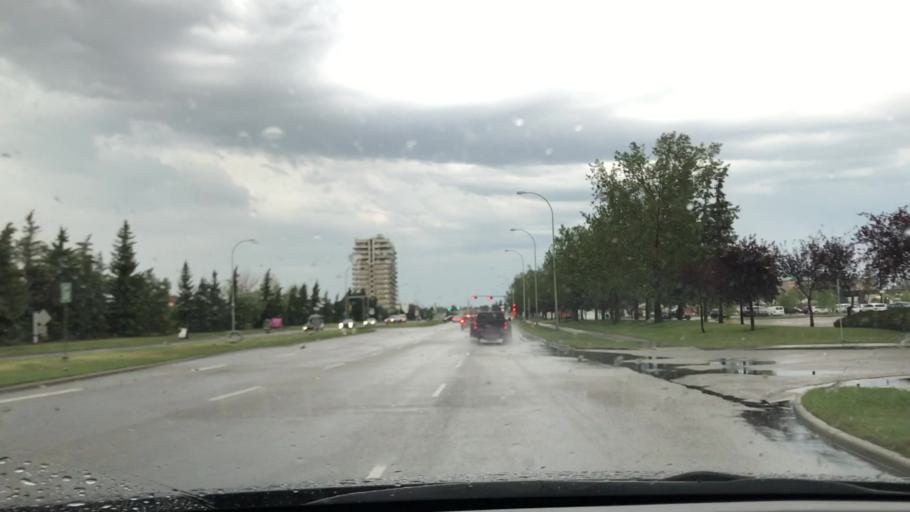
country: CA
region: Alberta
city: Edmonton
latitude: 53.4543
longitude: -113.4345
